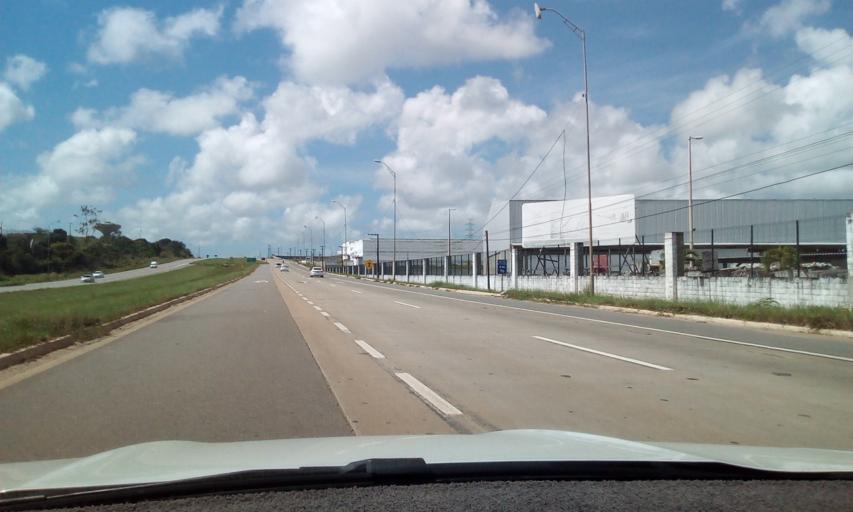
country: BR
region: Paraiba
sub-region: Conde
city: Conde
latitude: -7.2325
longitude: -34.9221
